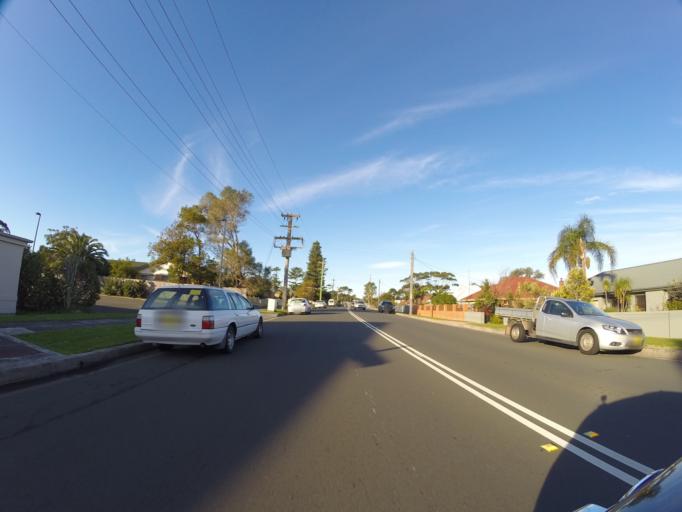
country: AU
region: New South Wales
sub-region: Wollongong
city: Bulli
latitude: -34.3299
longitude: 150.9148
